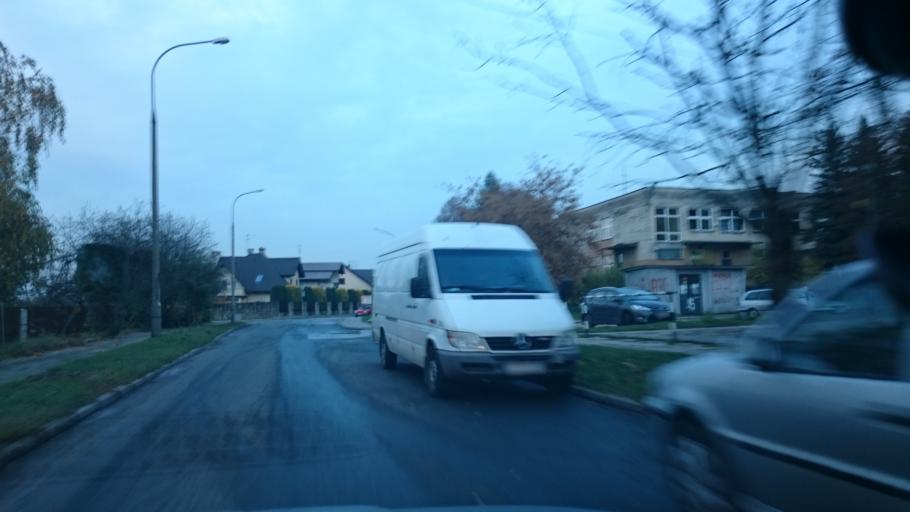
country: PL
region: Lesser Poland Voivodeship
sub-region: Powiat wielicki
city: Czarnochowice
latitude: 50.0202
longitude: 20.0152
